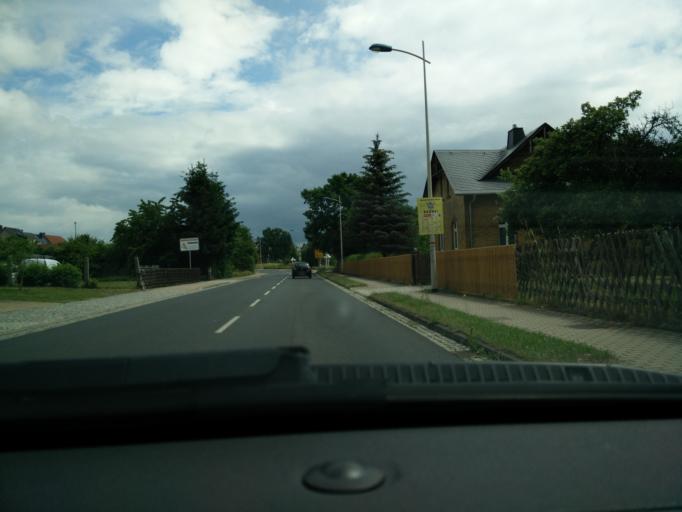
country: DE
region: Saxony
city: Bad Lausick
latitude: 51.1414
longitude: 12.6455
